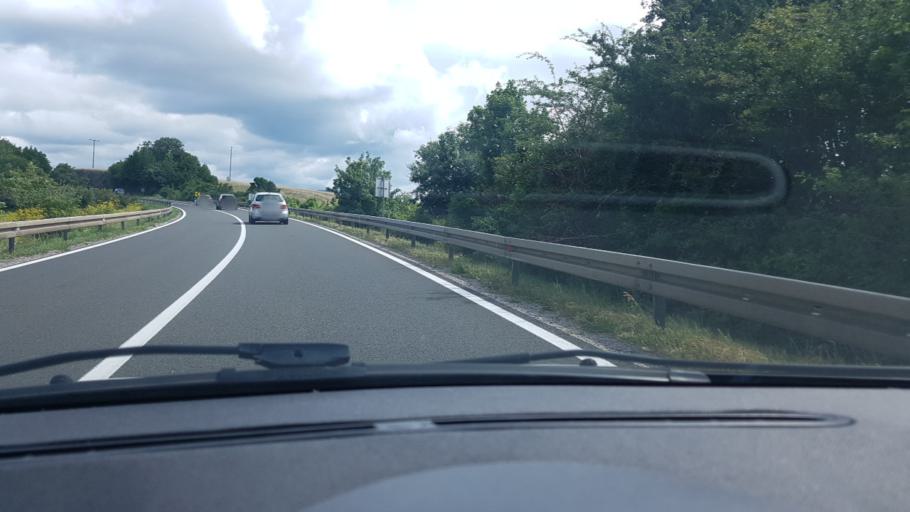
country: HR
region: Zadarska
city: Gracac
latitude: 44.4906
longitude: 15.7625
